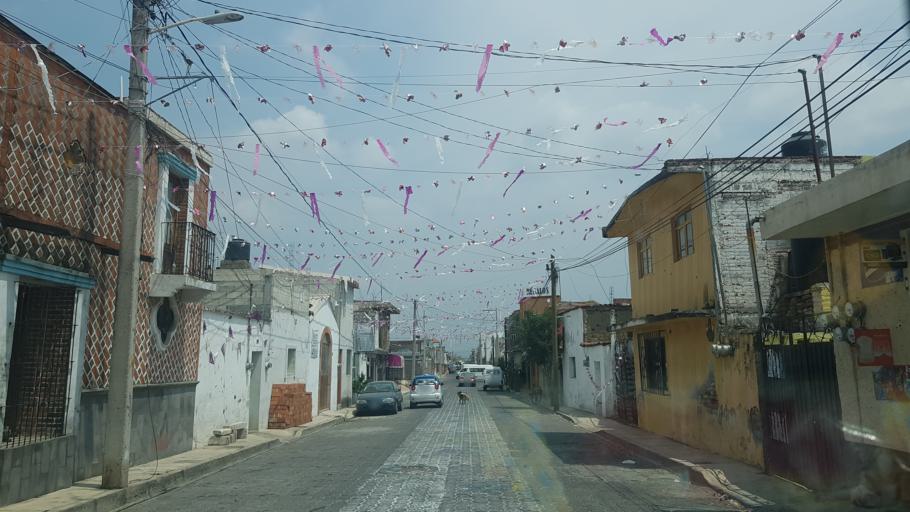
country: MX
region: Puebla
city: Huejotzingo
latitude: 19.1522
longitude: -98.4097
